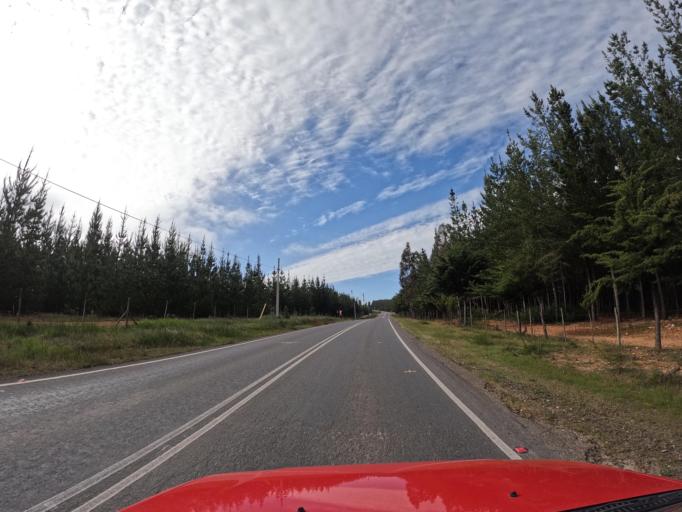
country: CL
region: O'Higgins
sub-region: Provincia de Colchagua
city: Santa Cruz
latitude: -34.3412
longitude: -71.8754
